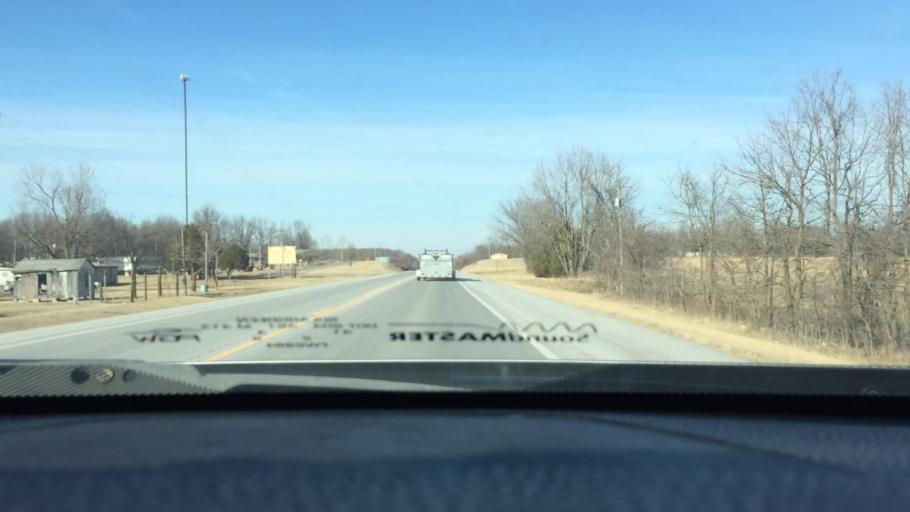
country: US
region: Missouri
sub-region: Newton County
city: Neosho
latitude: 36.8900
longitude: -94.3172
